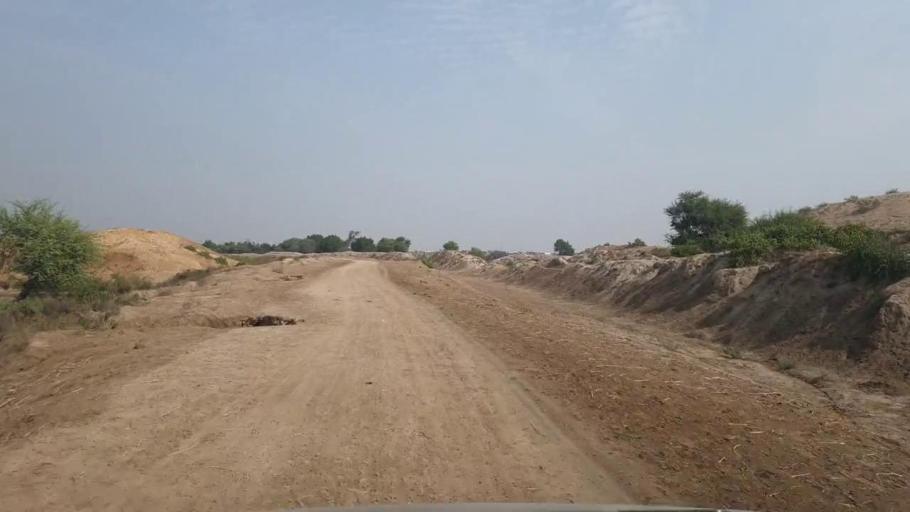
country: PK
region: Sindh
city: Tando Muhammad Khan
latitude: 25.1542
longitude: 68.4666
